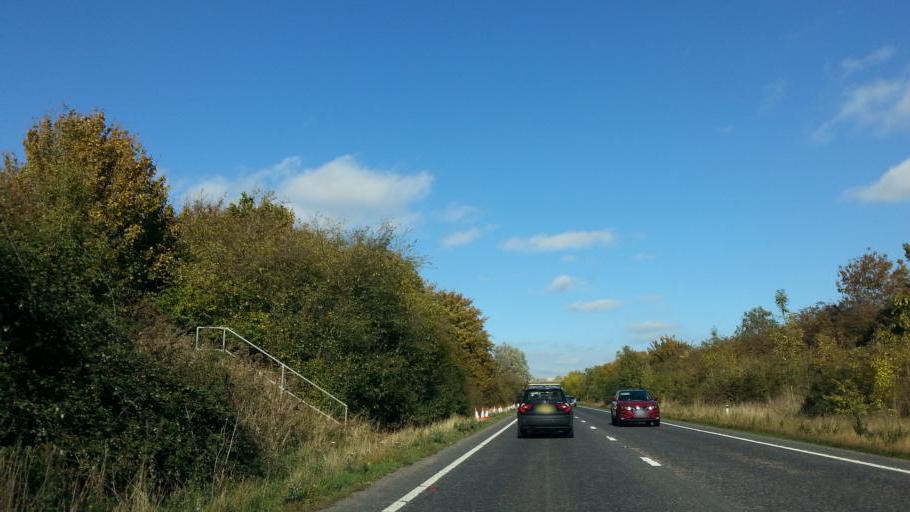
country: GB
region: England
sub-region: Northamptonshire
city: Thrapston
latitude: 52.3853
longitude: -0.5237
